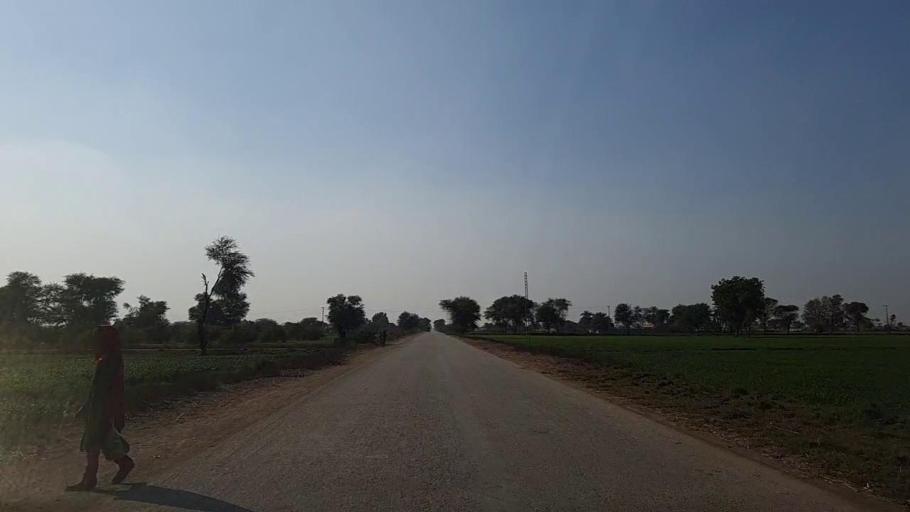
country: PK
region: Sindh
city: Daur
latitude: 26.4039
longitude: 68.3105
